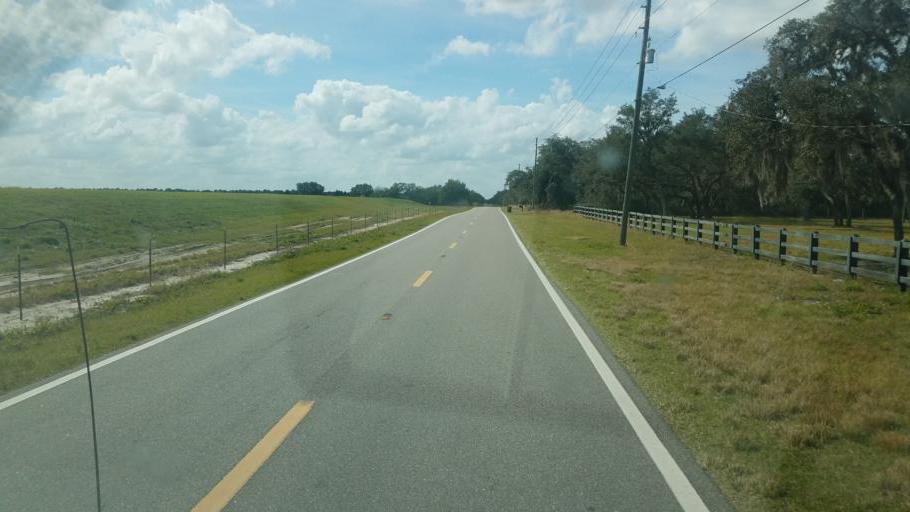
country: US
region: Florida
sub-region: Polk County
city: Lake Wales
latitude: 27.9253
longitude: -81.5096
